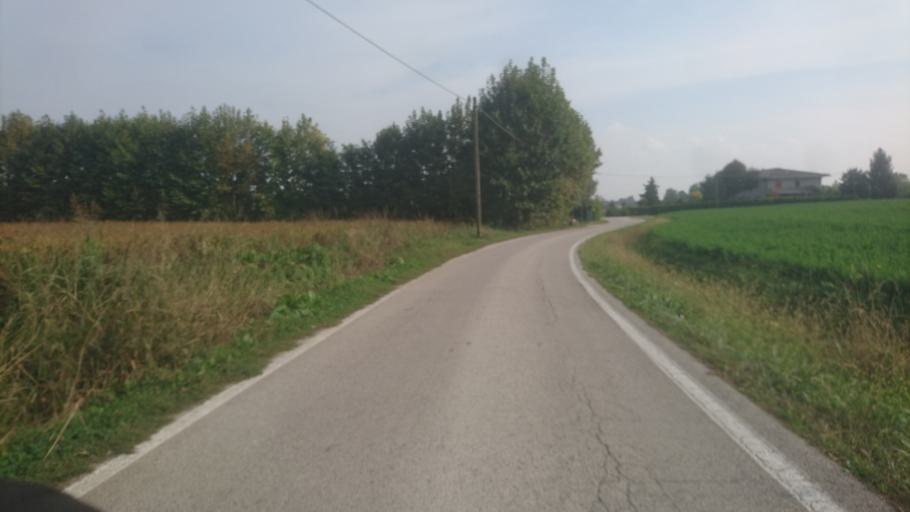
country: IT
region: Veneto
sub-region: Provincia di Vicenza
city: Montegalda
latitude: 45.4593
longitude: 11.6562
